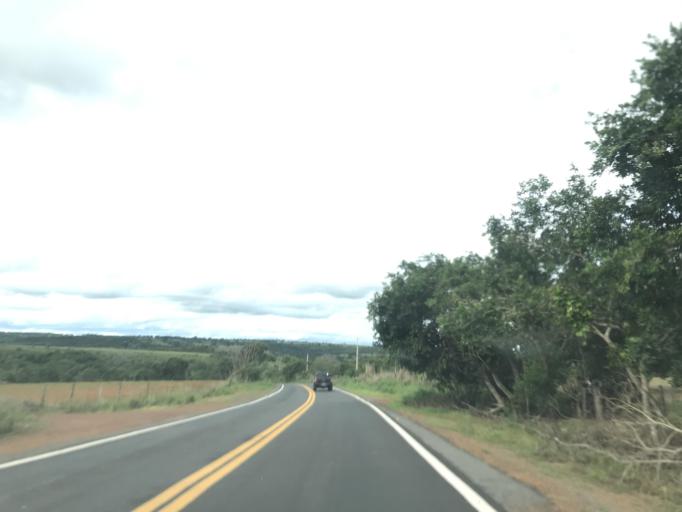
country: BR
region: Goias
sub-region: Bela Vista De Goias
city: Bela Vista de Goias
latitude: -17.1736
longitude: -48.6828
